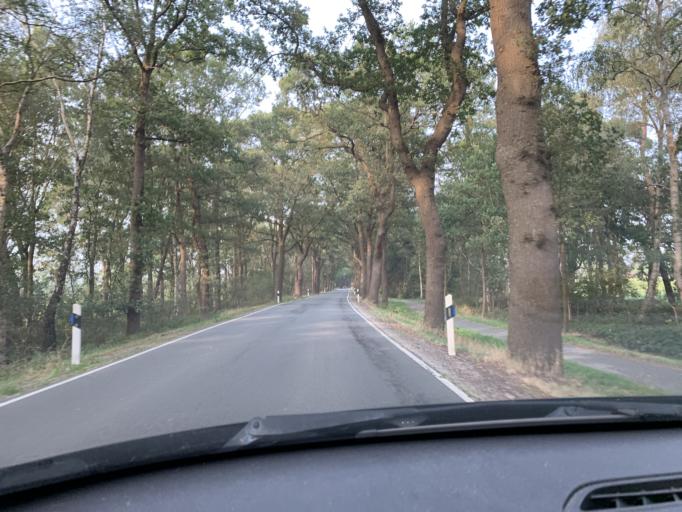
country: DE
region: Lower Saxony
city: Apen
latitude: 53.1918
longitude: 7.7850
